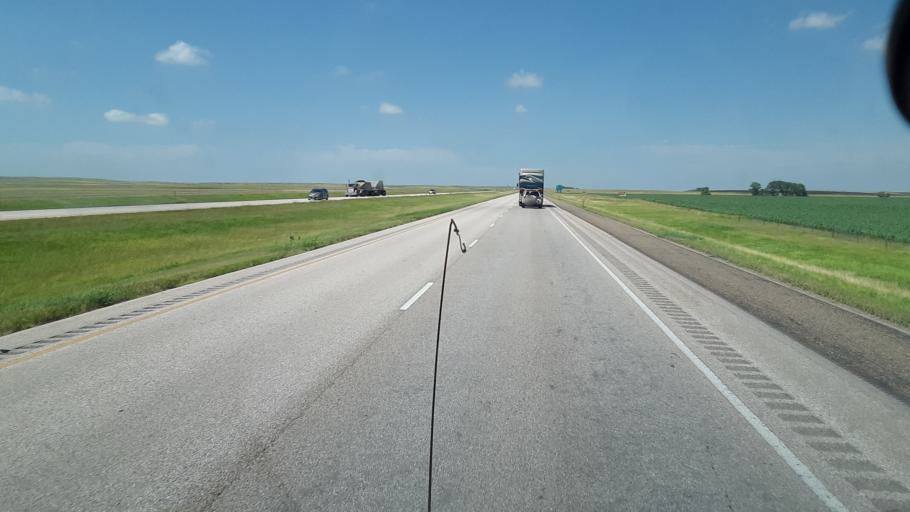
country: US
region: South Dakota
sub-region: Jackson County
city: Kadoka
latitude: 43.8364
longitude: -101.6281
